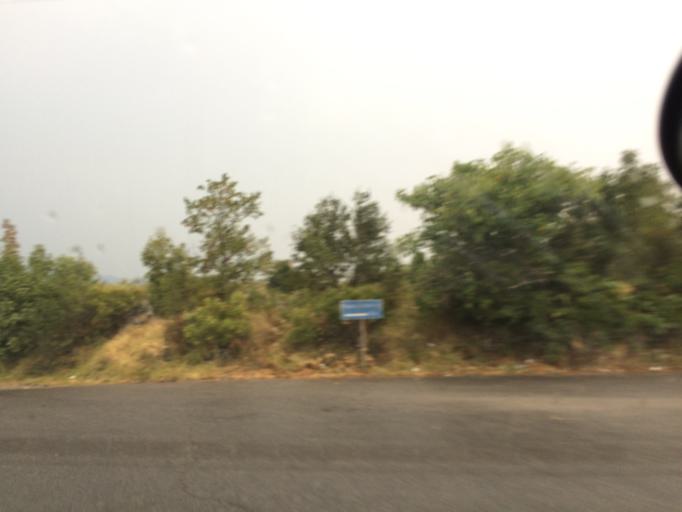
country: ME
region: Opstina Niksic
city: Niksic
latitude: 42.6773
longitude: 18.9737
